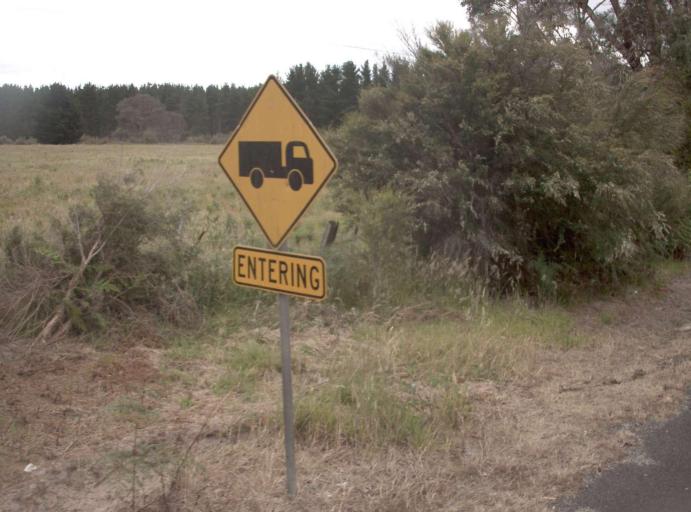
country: AU
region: Victoria
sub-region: Wellington
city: Sale
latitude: -38.2212
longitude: 147.0581
